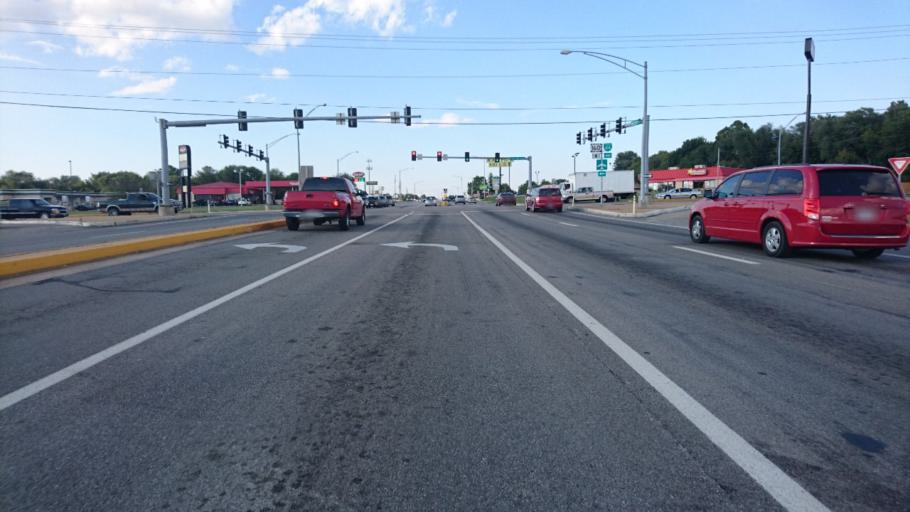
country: US
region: Missouri
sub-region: Greene County
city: Springfield
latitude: 37.2117
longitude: -93.3488
